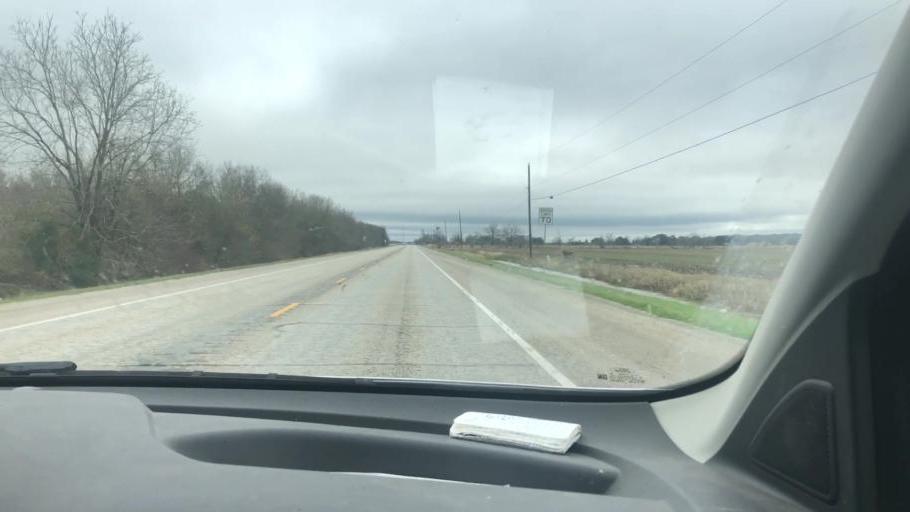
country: US
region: Texas
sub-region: Wharton County
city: Wharton
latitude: 29.2612
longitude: -96.0550
